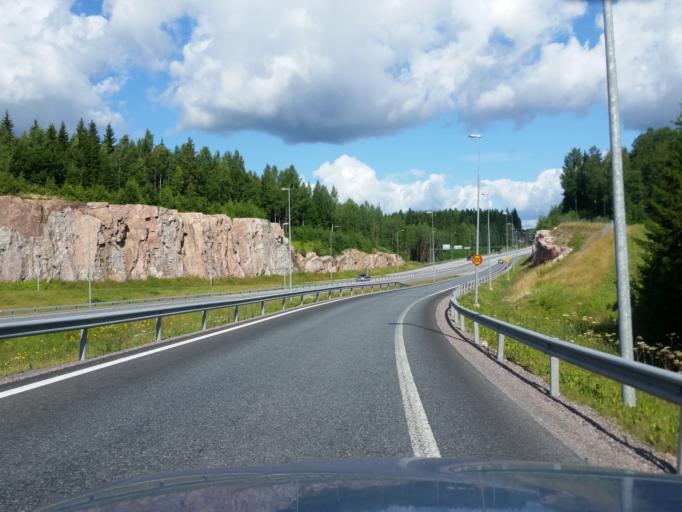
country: FI
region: Uusimaa
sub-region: Helsinki
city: Vihti
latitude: 60.2943
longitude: 24.3666
